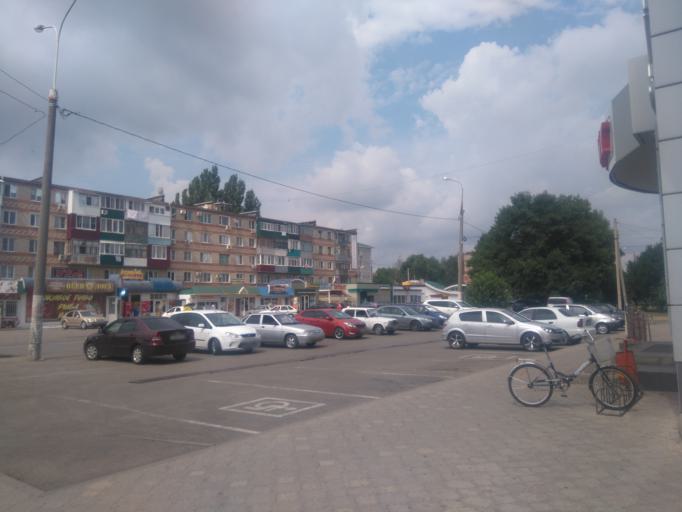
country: RU
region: Krasnodarskiy
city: Tikhoretsk
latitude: 45.8549
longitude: 40.1373
